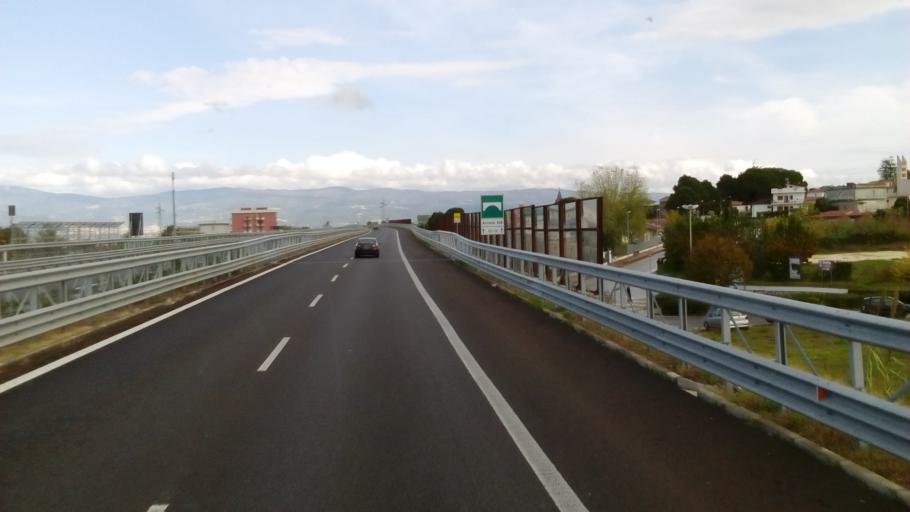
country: IT
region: Calabria
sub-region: Provincia di Catanzaro
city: Acconia
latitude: 38.8362
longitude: 16.2590
